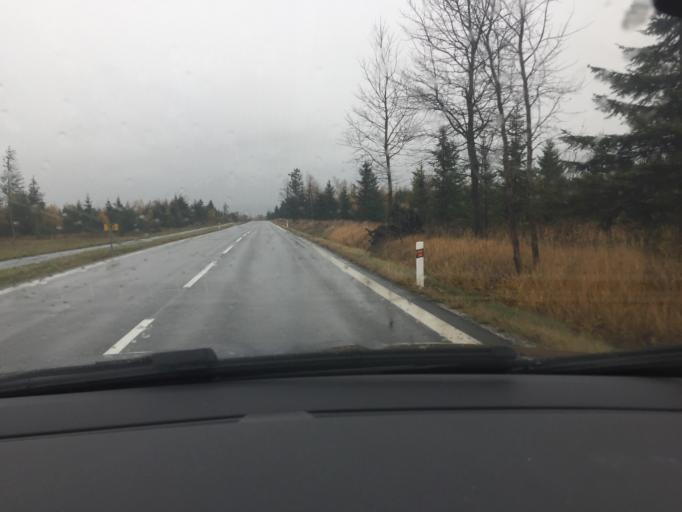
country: SK
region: Presovsky
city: Spisska Bela
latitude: 49.2130
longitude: 20.3563
